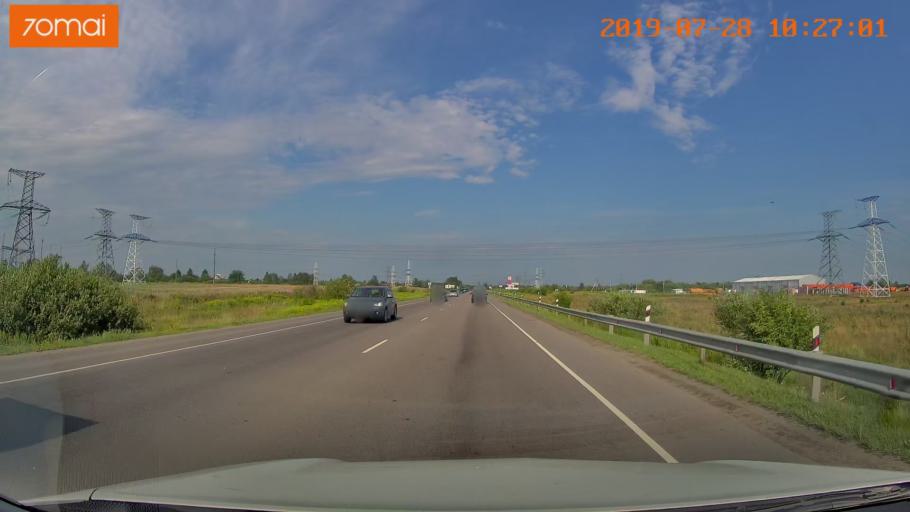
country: RU
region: Kaliningrad
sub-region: Gorod Kaliningrad
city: Kaliningrad
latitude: 54.7695
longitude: 20.5249
